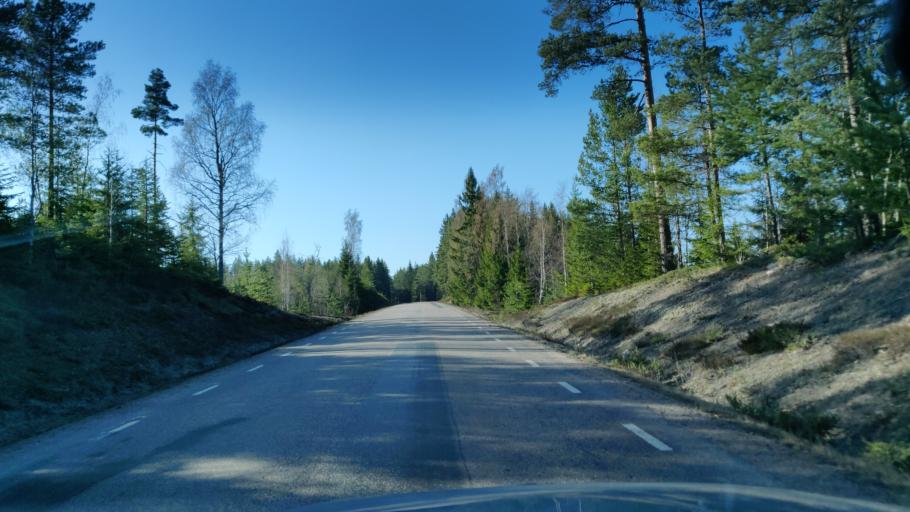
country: SE
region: Vaermland
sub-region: Sunne Kommun
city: Sunne
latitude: 59.9895
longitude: 13.3114
